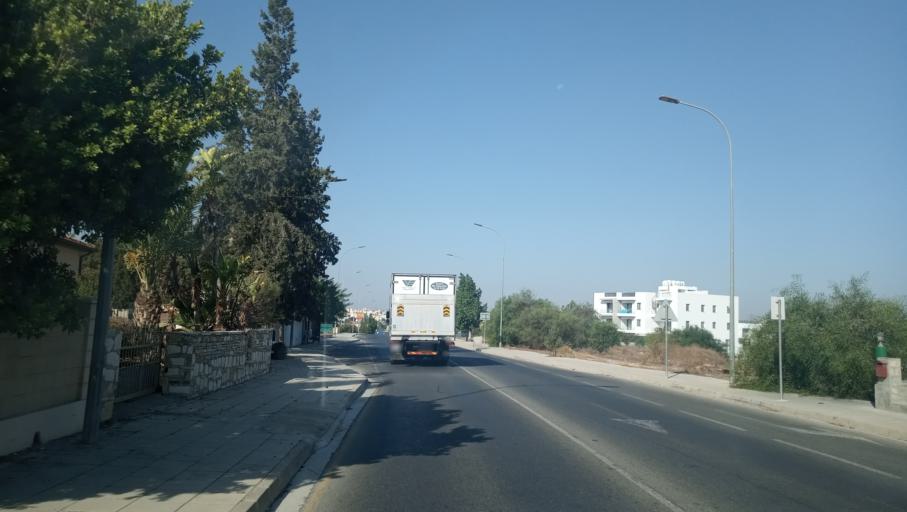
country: CY
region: Lefkosia
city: Geri
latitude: 35.1074
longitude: 33.4025
